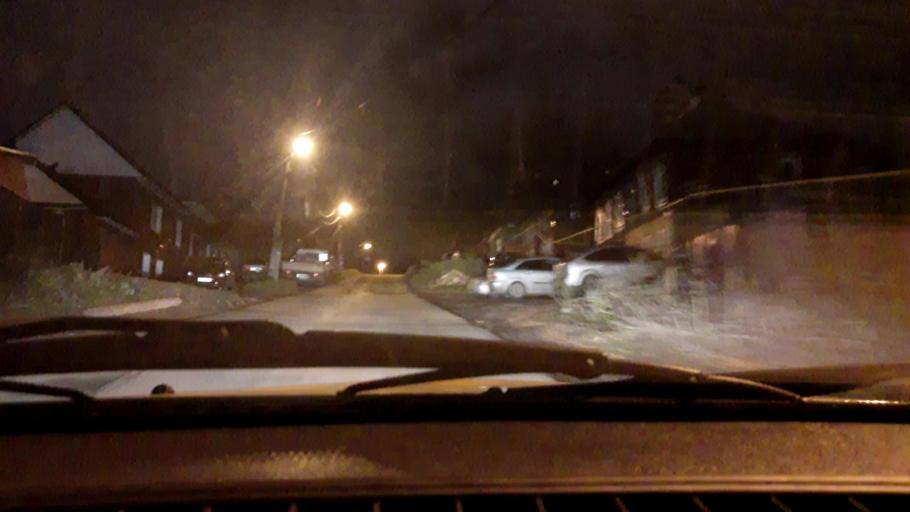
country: RU
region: Bashkortostan
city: Ufa
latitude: 54.7394
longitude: 55.9326
